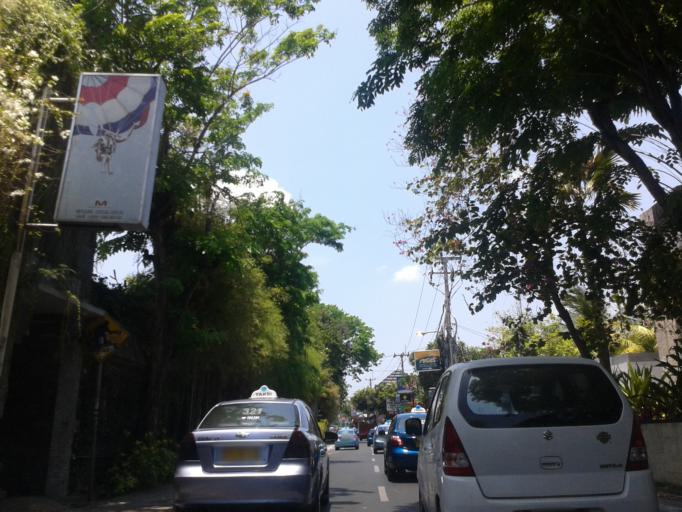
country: ID
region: Bali
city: Kuta
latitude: -8.7090
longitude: 115.1679
